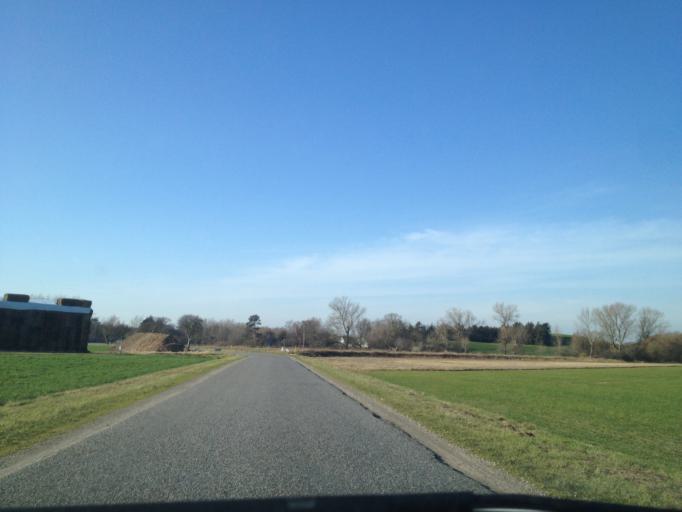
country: DK
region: South Denmark
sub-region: Kerteminde Kommune
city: Kerteminde
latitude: 55.5500
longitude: 10.6296
